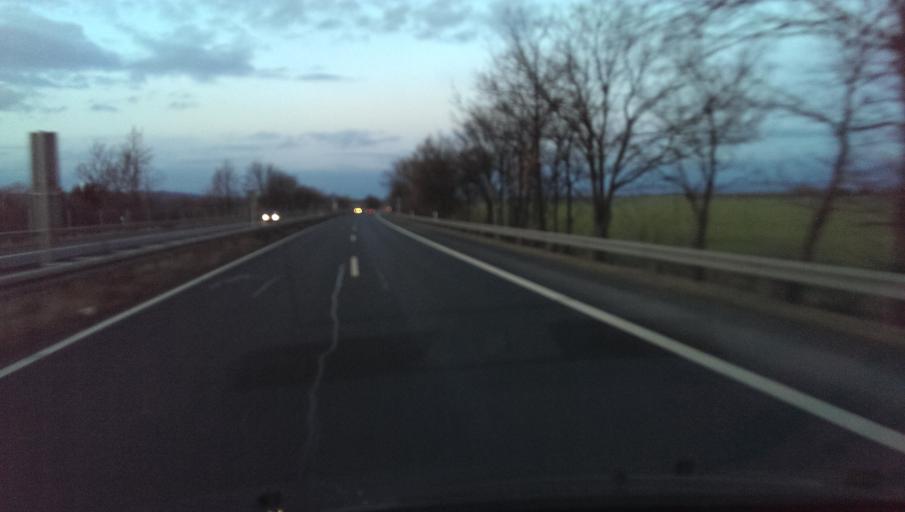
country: DE
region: Lower Saxony
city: Vienenburg
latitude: 51.9200
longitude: 10.5564
